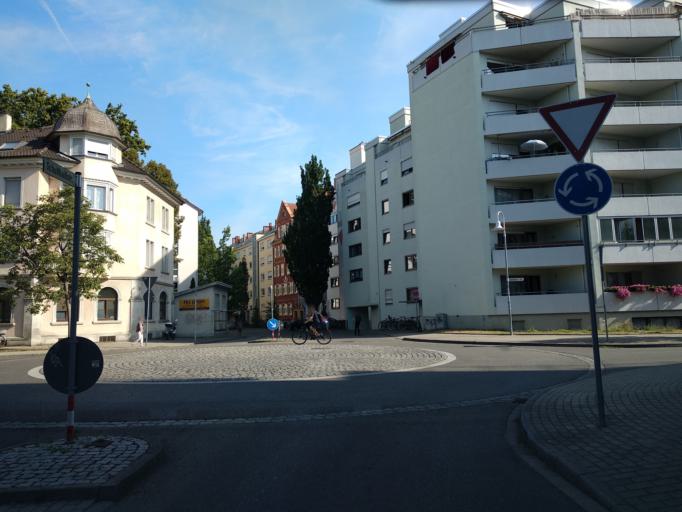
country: DE
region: Baden-Wuerttemberg
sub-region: Freiburg Region
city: Konstanz
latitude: 47.6621
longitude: 9.1666
